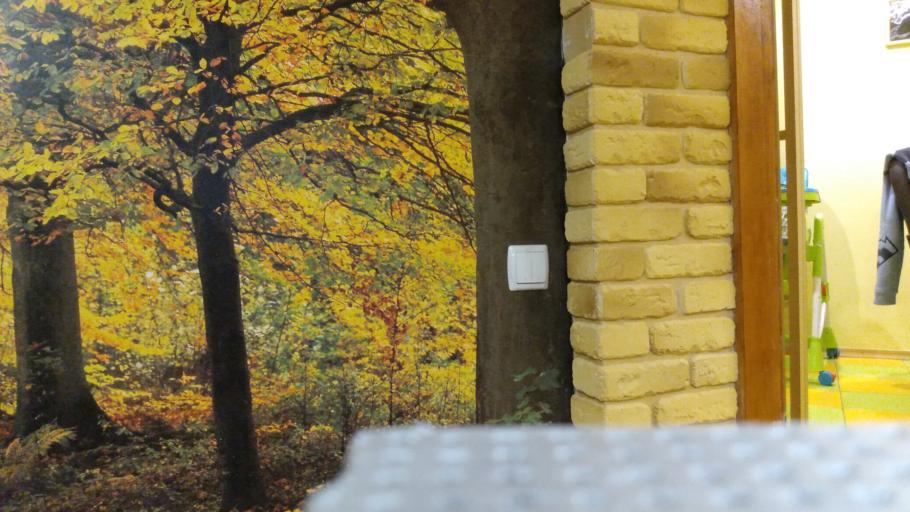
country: RU
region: Vologda
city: Babayevo
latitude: 59.3612
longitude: 36.0022
